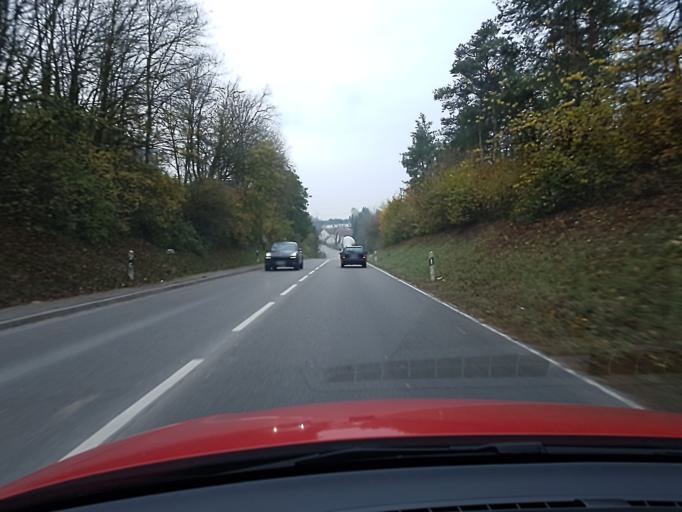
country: DE
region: Baden-Wuerttemberg
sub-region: Regierungsbezirk Stuttgart
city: Talheim
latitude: 49.0987
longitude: 9.1844
